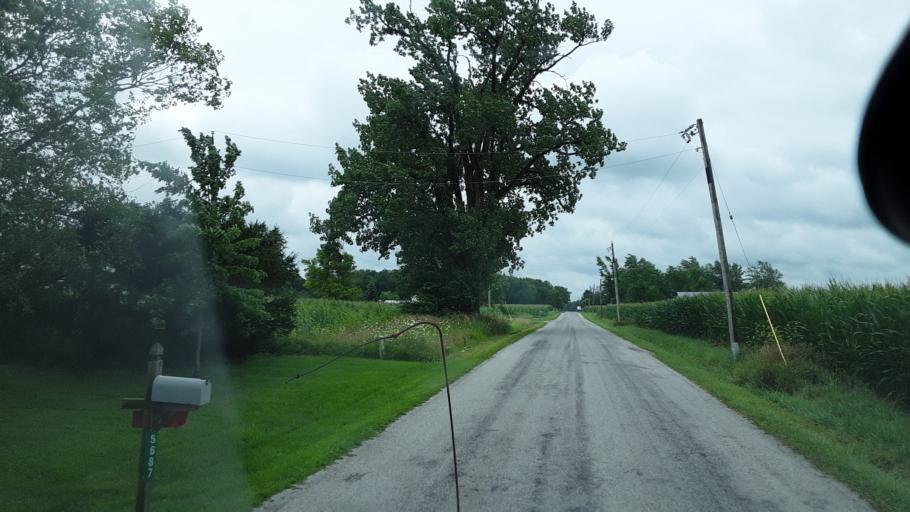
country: US
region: Indiana
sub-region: Wells County
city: Ossian
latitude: 40.8266
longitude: -85.0721
